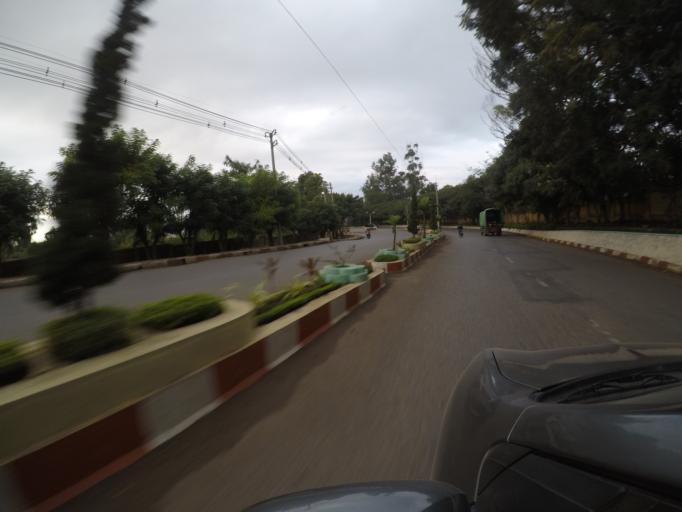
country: MM
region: Shan
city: Taunggyi
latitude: 20.8105
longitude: 97.0357
